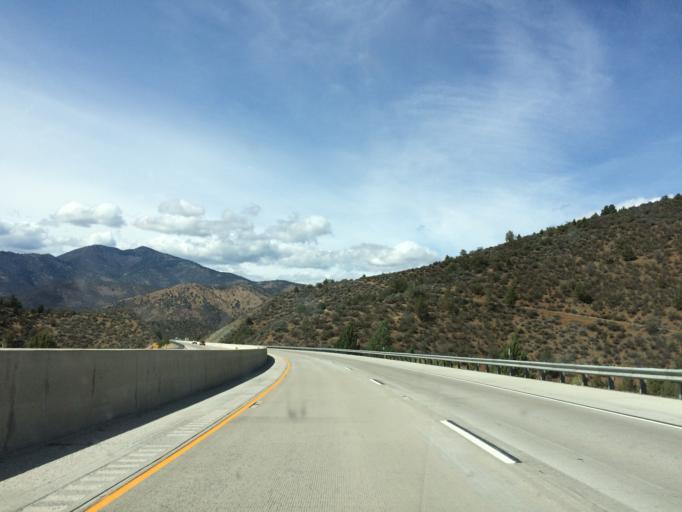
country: US
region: California
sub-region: Siskiyou County
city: Montague
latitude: 41.8120
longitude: -122.5722
